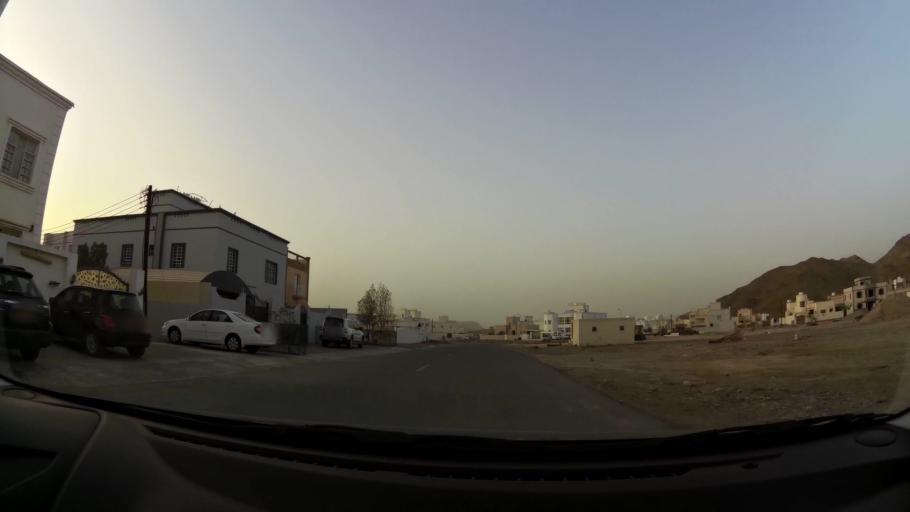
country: OM
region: Muhafazat Masqat
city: Bawshar
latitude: 23.4748
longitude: 58.3067
